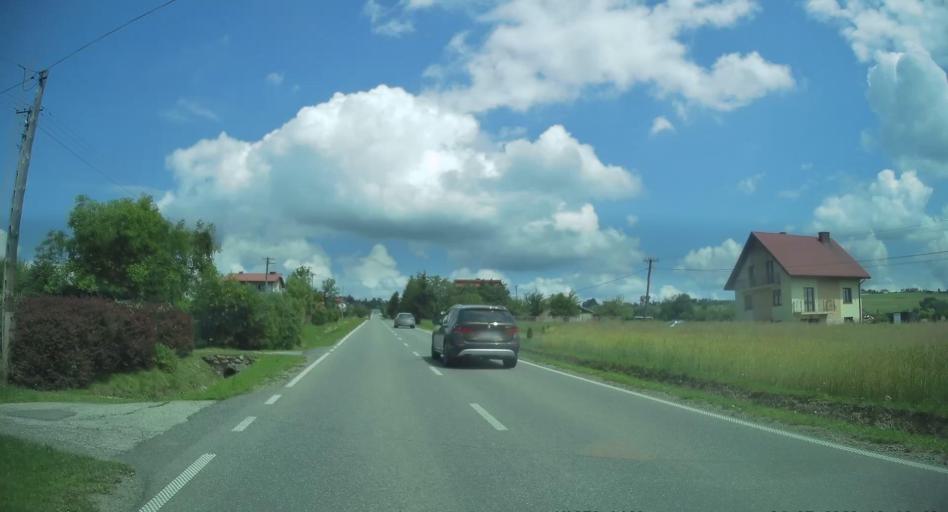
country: PL
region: Lesser Poland Voivodeship
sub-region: Powiat nowosadecki
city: Korzenna
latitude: 49.6796
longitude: 20.7761
